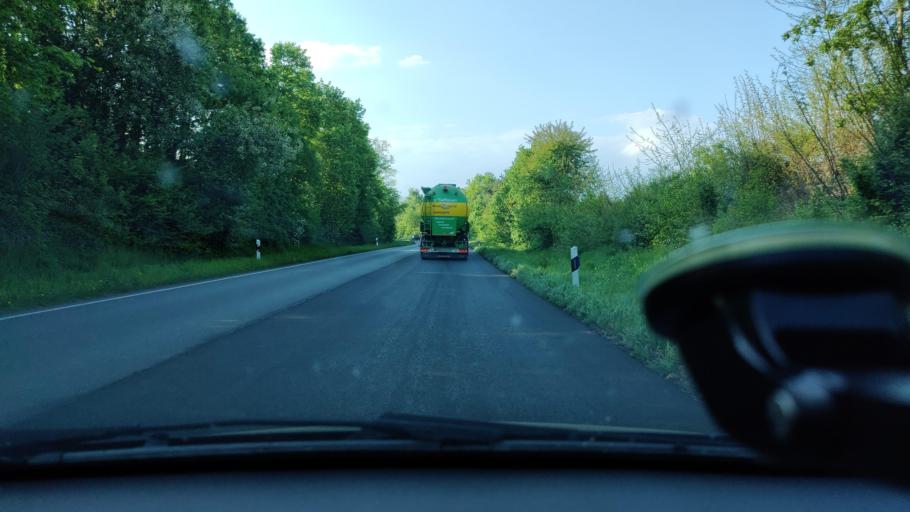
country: DE
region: North Rhine-Westphalia
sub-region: Regierungsbezirk Munster
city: Telgte
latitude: 51.9873
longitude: 7.8088
